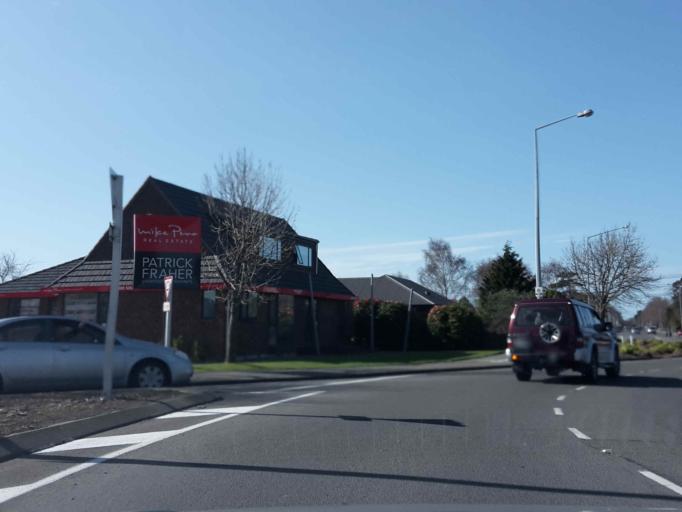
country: NZ
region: Canterbury
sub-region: Selwyn District
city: Prebbleton
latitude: -43.5393
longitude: 172.5536
